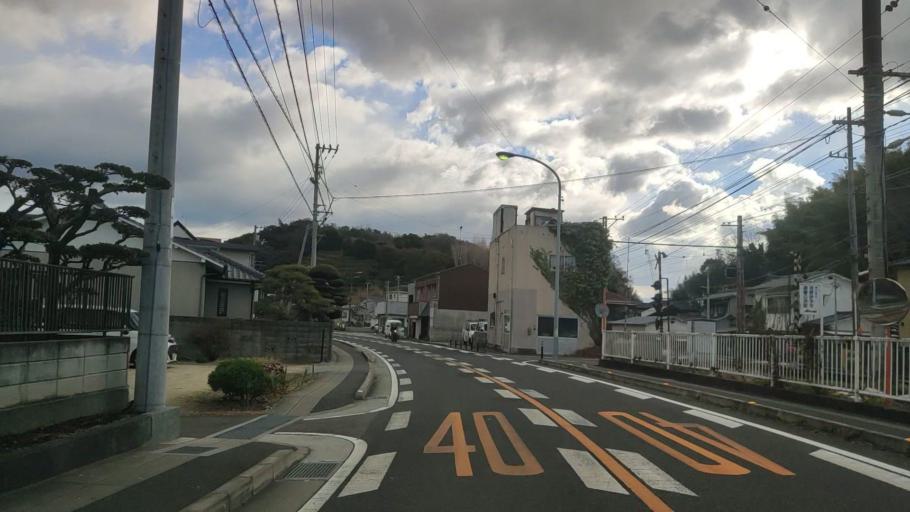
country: JP
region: Ehime
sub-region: Shikoku-chuo Shi
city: Matsuyama
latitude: 33.8699
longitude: 132.7113
